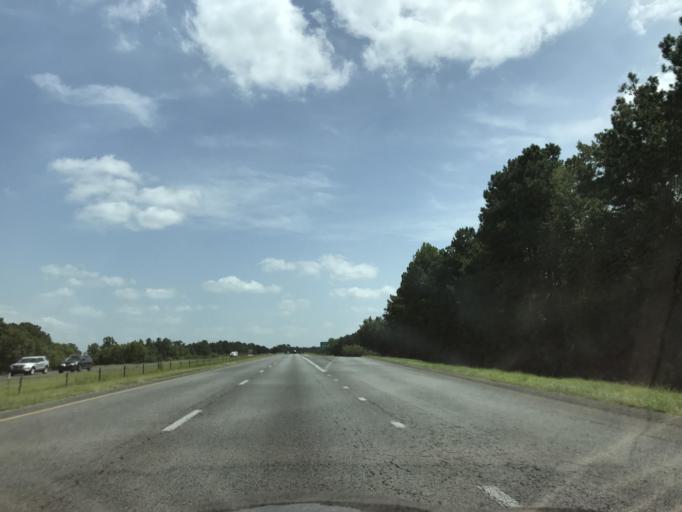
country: US
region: North Carolina
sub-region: Duplin County
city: Wallace
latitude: 34.7580
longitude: -77.9536
